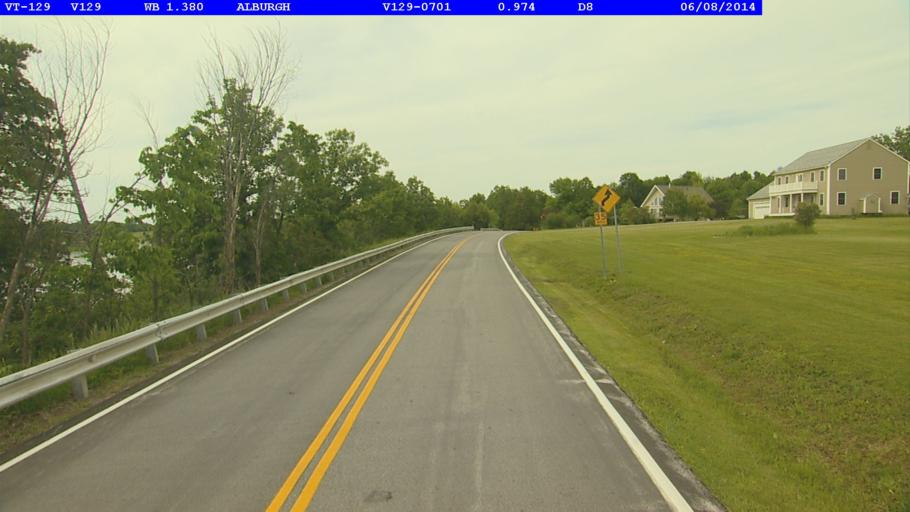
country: US
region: Vermont
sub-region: Grand Isle County
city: North Hero
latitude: 44.8974
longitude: -73.3041
